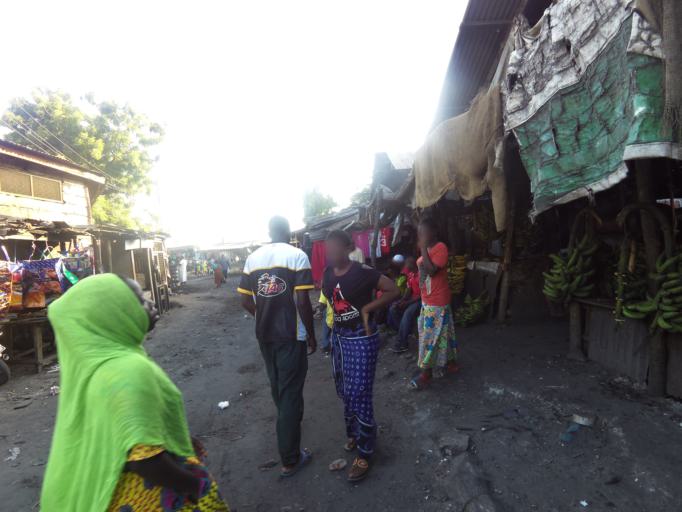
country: TZ
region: Dar es Salaam
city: Magomeni
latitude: -6.7688
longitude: 39.2662
